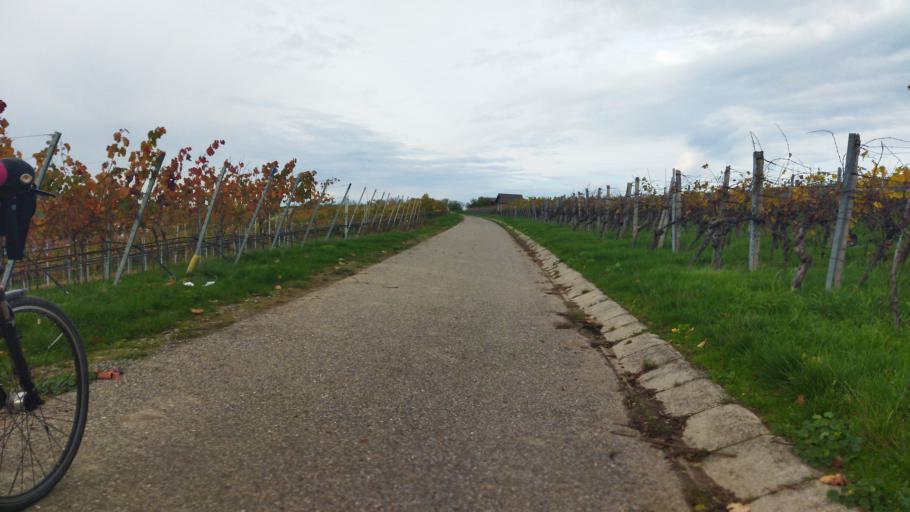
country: DE
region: Baden-Wuerttemberg
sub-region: Regierungsbezirk Stuttgart
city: Gemmrigheim
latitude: 49.0359
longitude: 9.1586
